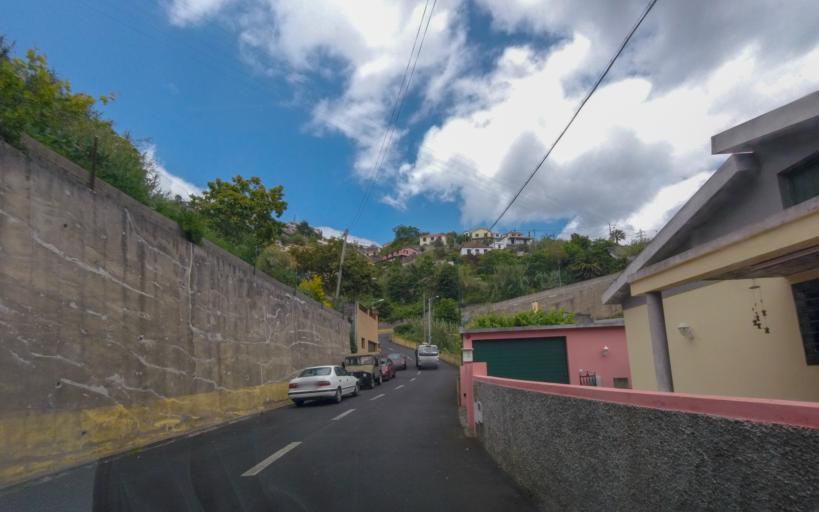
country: PT
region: Madeira
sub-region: Funchal
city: Nossa Senhora do Monte
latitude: 32.6632
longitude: -16.8824
